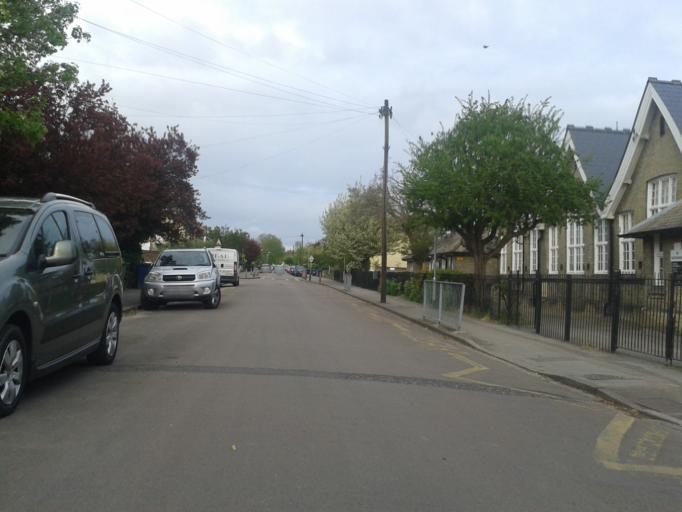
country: GB
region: England
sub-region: Cambridgeshire
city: Cambridge
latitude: 52.1863
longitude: 0.1454
